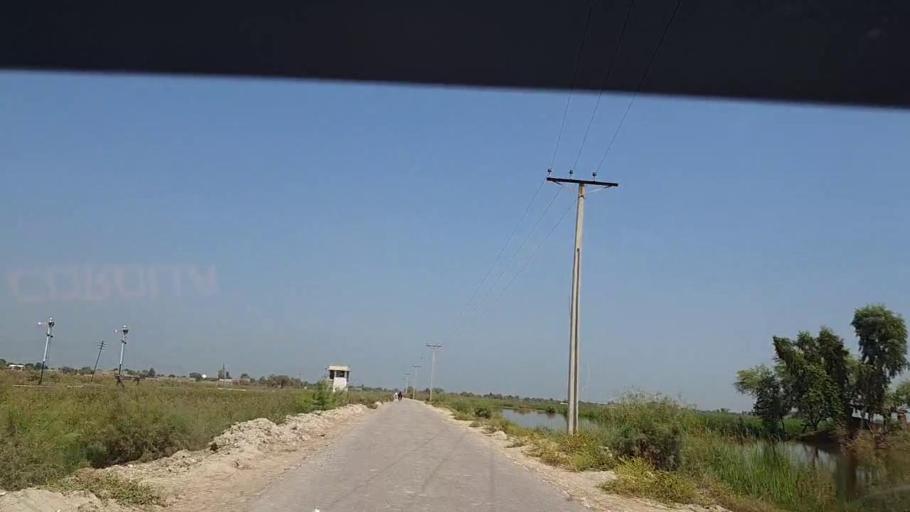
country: PK
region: Sindh
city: Tangwani
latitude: 28.2800
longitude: 69.0063
